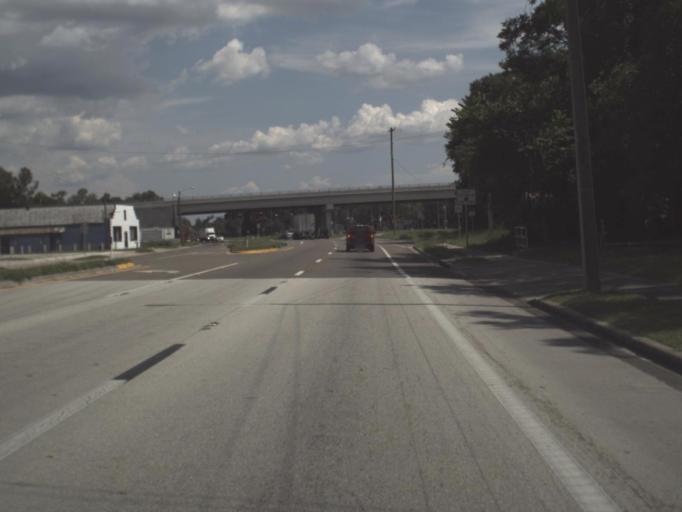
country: US
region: Florida
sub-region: Alachua County
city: Hawthorne
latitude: 29.5985
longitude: -82.0870
